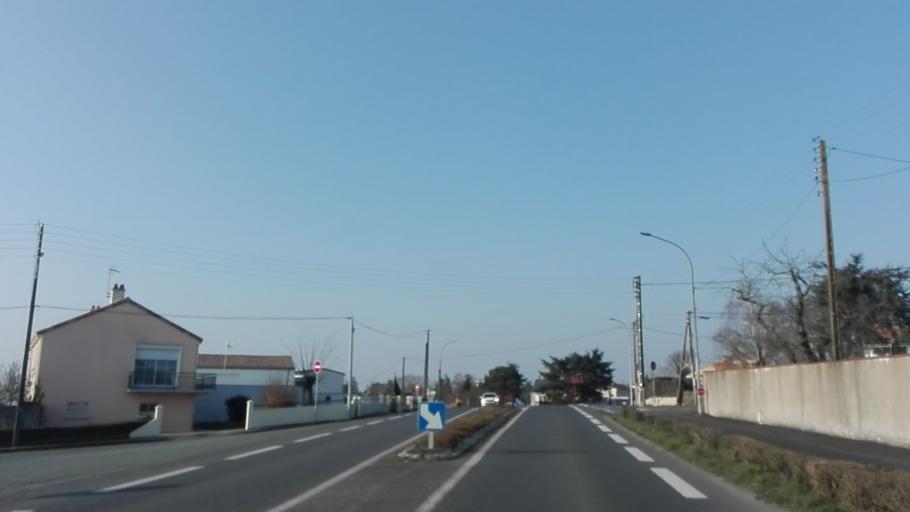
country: FR
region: Pays de la Loire
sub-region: Departement de la Vendee
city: Montaigu
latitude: 46.9676
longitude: -1.3080
